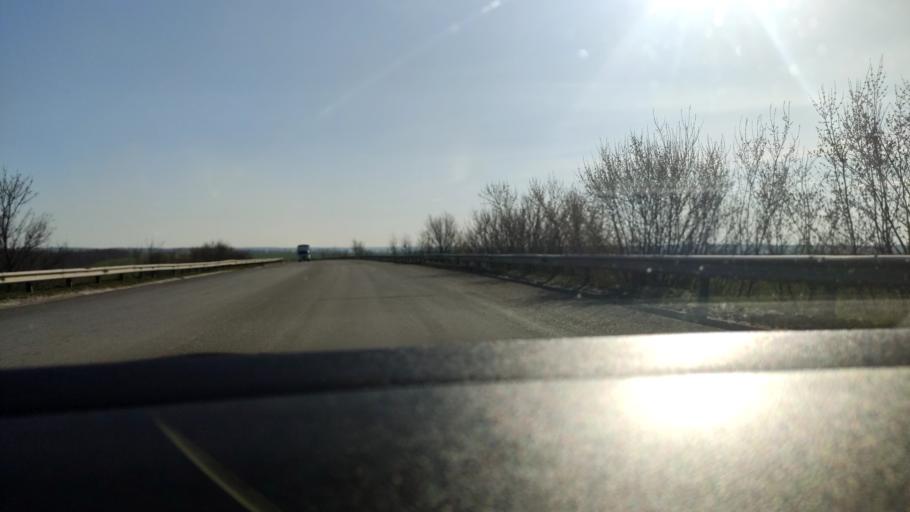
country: RU
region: Voronezj
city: Kolodeznyy
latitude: 51.4089
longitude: 39.2473
